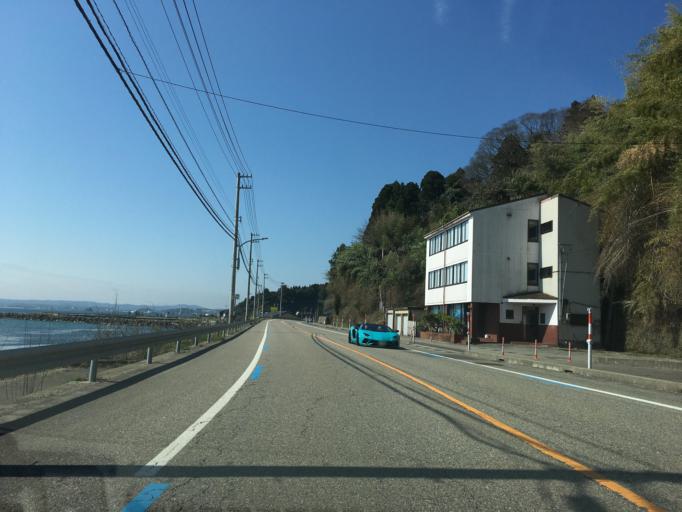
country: JP
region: Toyama
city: Himi
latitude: 36.8989
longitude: 137.0097
